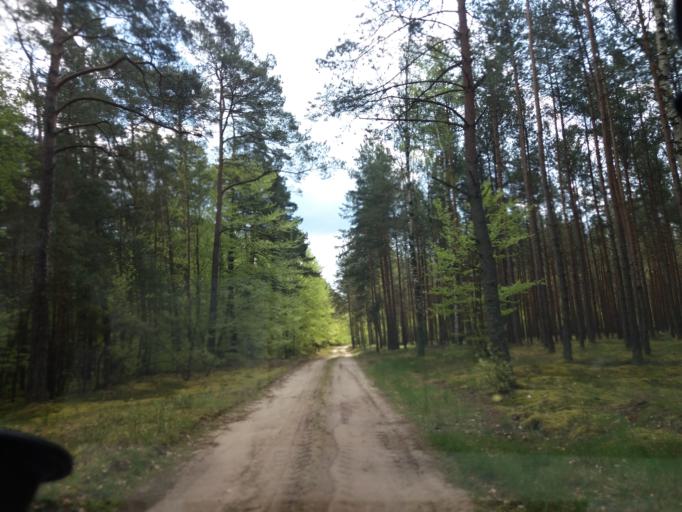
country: PL
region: West Pomeranian Voivodeship
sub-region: Powiat choszczenski
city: Drawno
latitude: 53.1529
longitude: 15.8071
